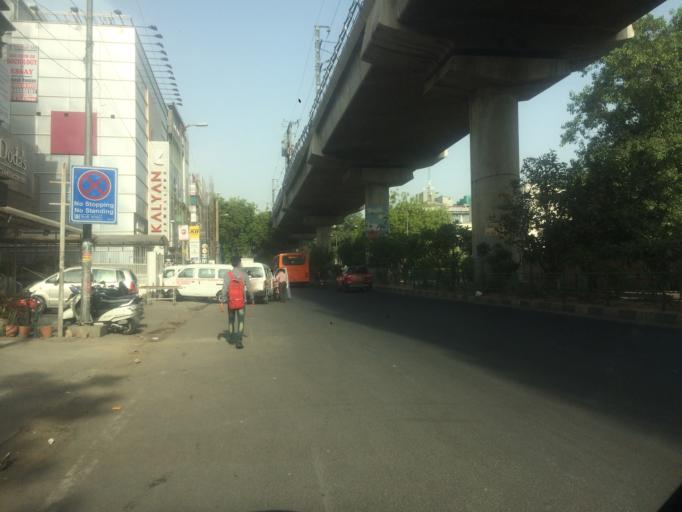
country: IN
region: NCT
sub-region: Central Delhi
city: Karol Bagh
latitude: 28.6436
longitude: 77.1865
